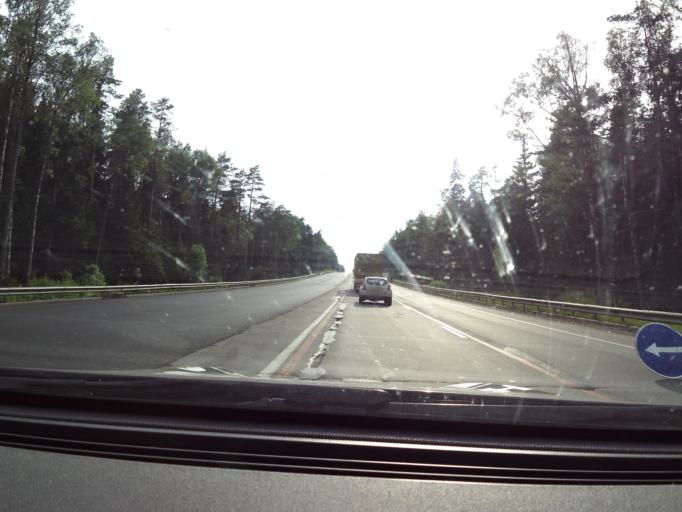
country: RU
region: Vladimir
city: Stepantsevo
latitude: 56.2317
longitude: 41.7650
